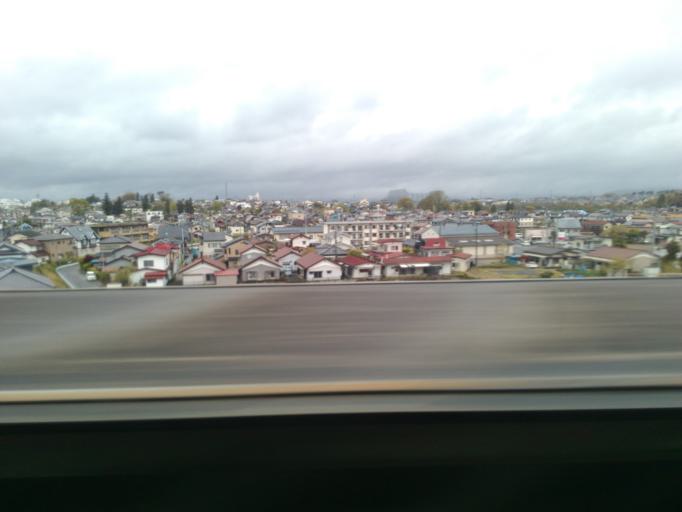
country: JP
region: Fukushima
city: Koriyama
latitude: 37.4256
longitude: 140.3972
